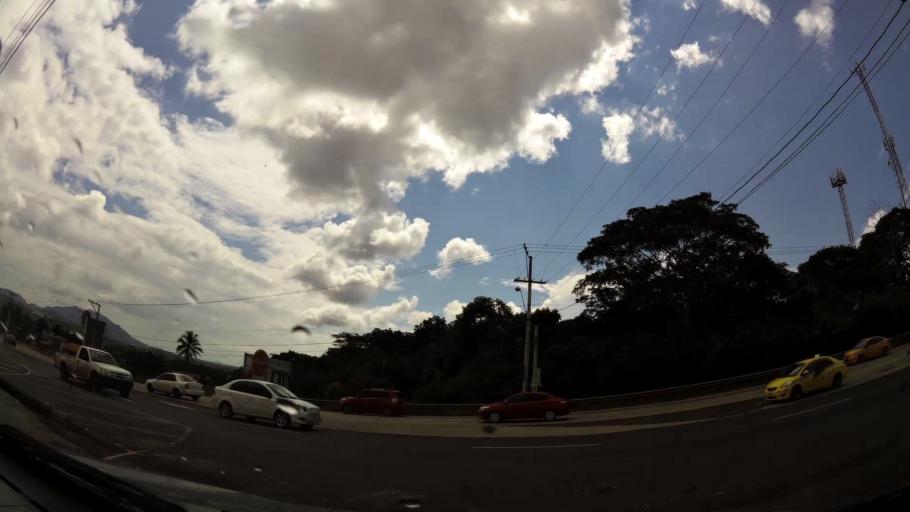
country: PA
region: Panama
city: Nuevo Arraijan
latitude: 8.9235
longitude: -79.7364
